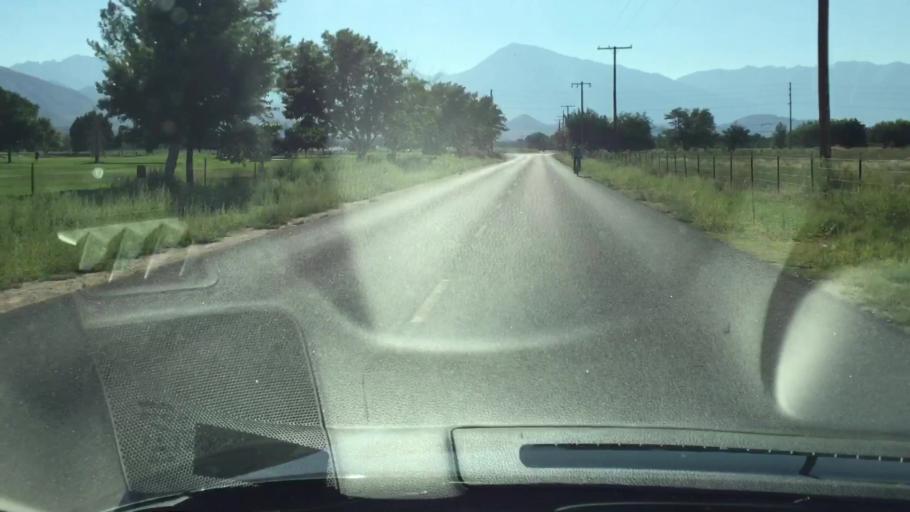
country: US
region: California
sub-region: Inyo County
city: Bishop
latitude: 37.3468
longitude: -118.4021
